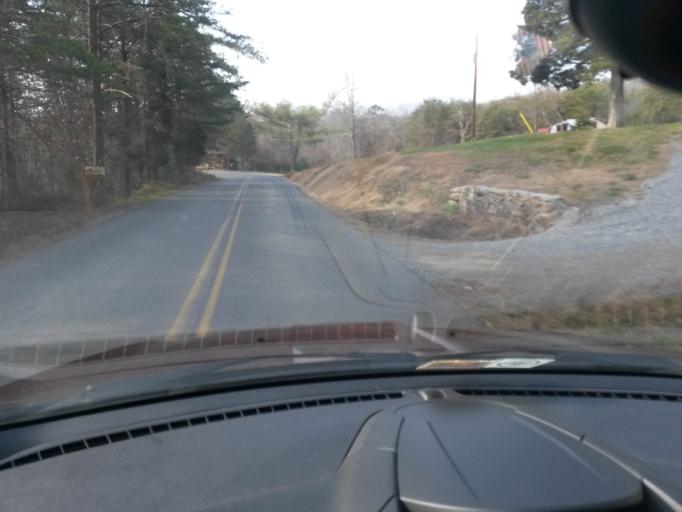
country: US
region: Virginia
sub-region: Botetourt County
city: Fincastle
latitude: 37.5495
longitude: -79.8774
